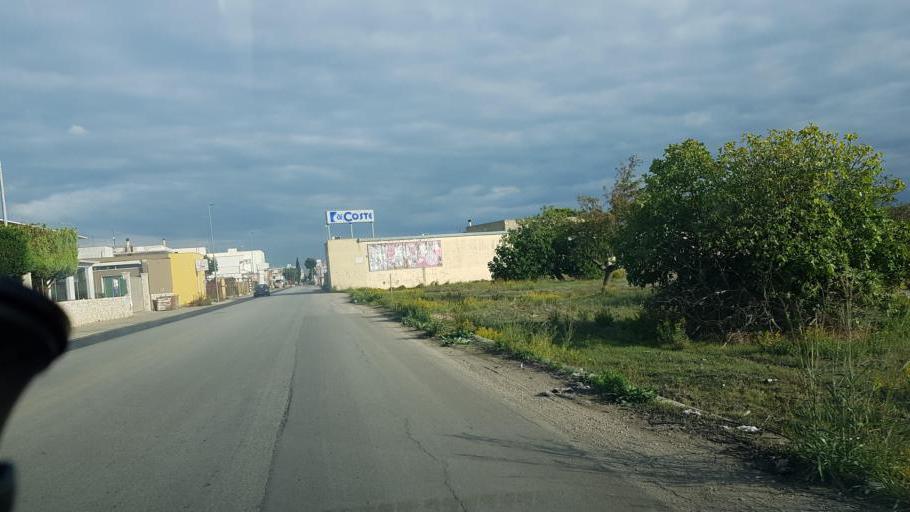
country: IT
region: Apulia
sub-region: Provincia di Brindisi
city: Francavilla Fontana
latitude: 40.5302
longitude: 17.5701
